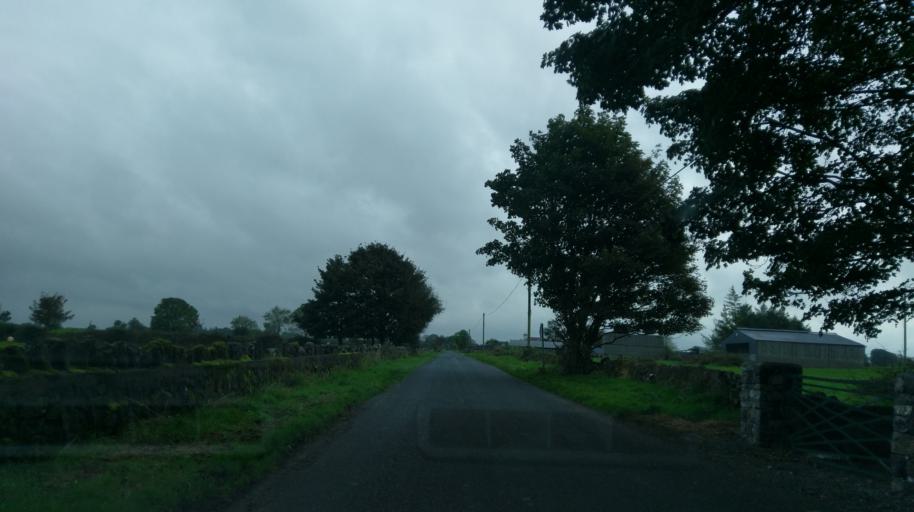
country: IE
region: Connaught
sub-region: County Galway
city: Athenry
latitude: 53.4564
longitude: -8.6014
